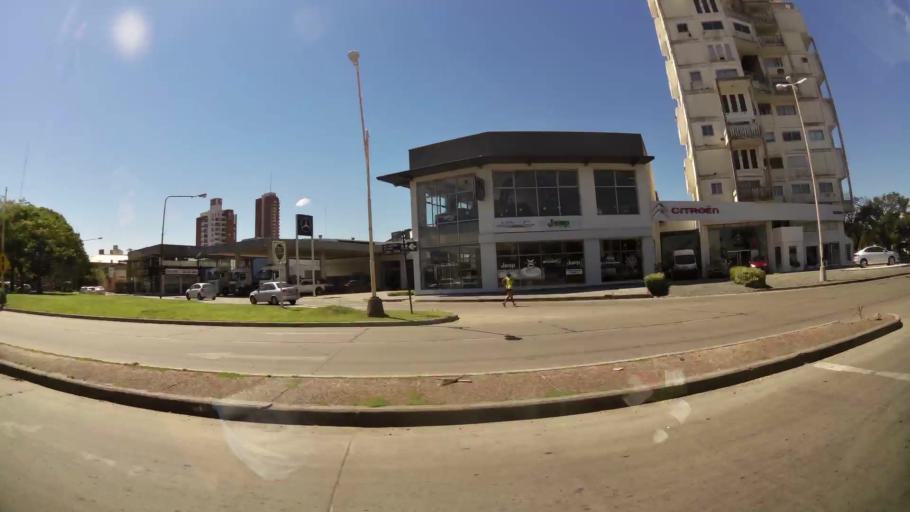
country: AR
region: Santa Fe
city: Santa Fe de la Vera Cruz
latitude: -31.6470
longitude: -60.7023
